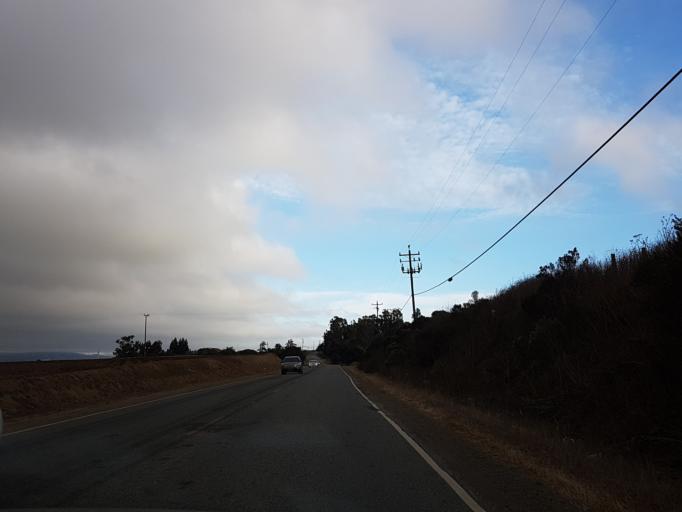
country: US
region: California
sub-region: Monterey County
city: Salinas
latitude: 36.5950
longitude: -121.6180
